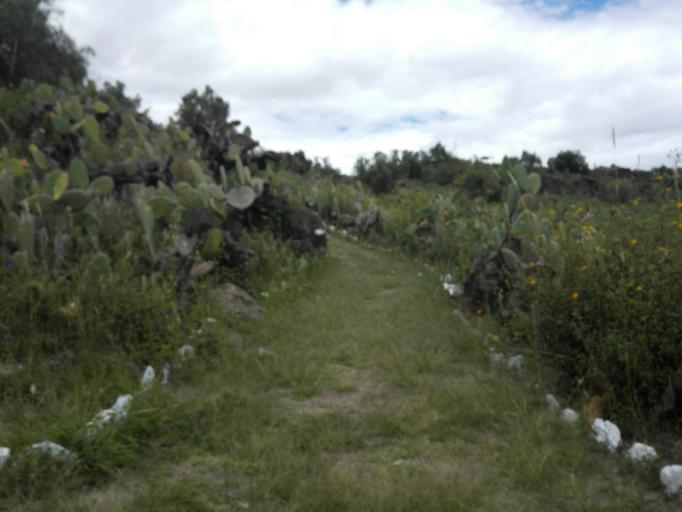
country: PE
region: Ayacucho
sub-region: Provincia de Huamanga
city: Pacaycasa
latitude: -13.0651
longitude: -74.1932
